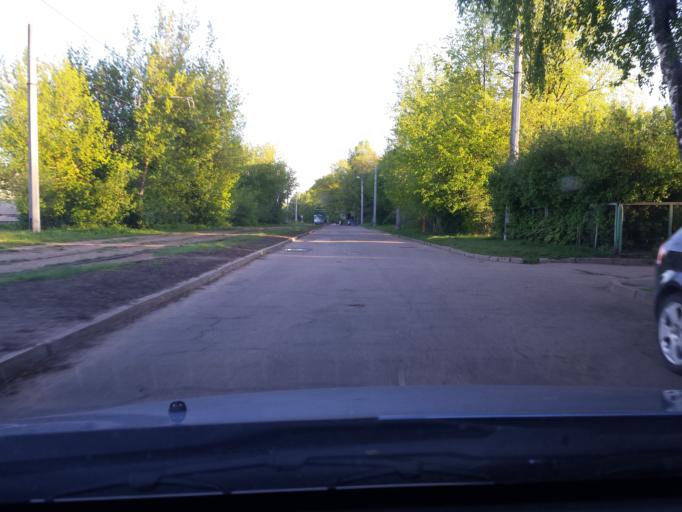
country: LV
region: Riga
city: Jaunciems
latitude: 57.0083
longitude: 24.1255
